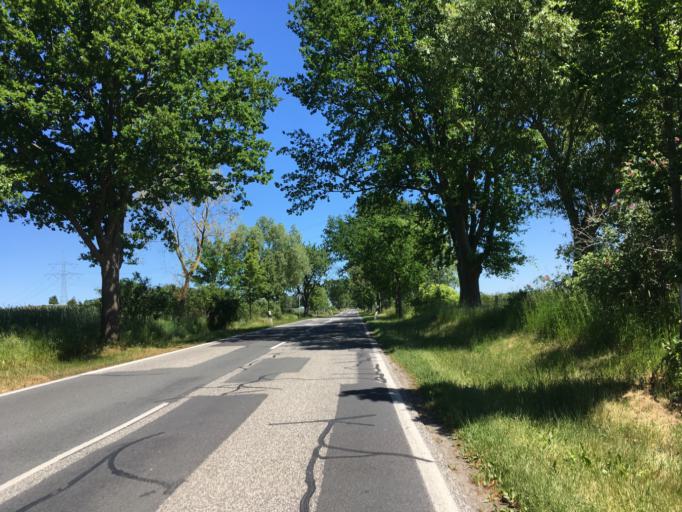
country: DE
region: Brandenburg
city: Zehdenick
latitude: 52.9394
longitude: 13.2680
